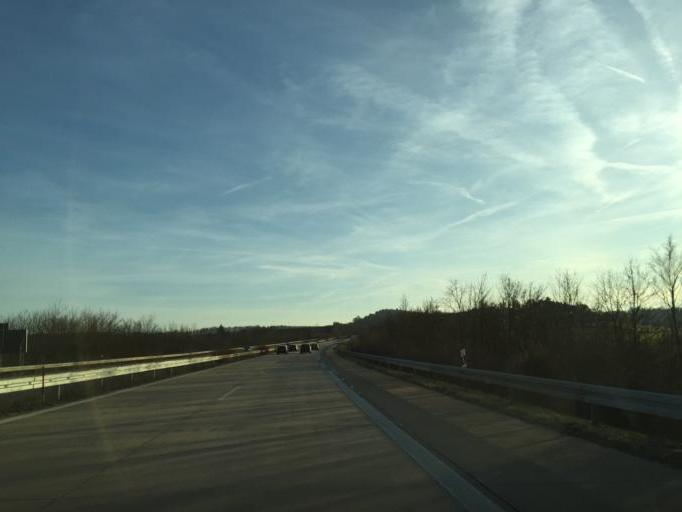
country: DE
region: Bavaria
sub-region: Regierungsbezirk Mittelfranken
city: Neusitz
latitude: 49.3503
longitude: 10.2218
